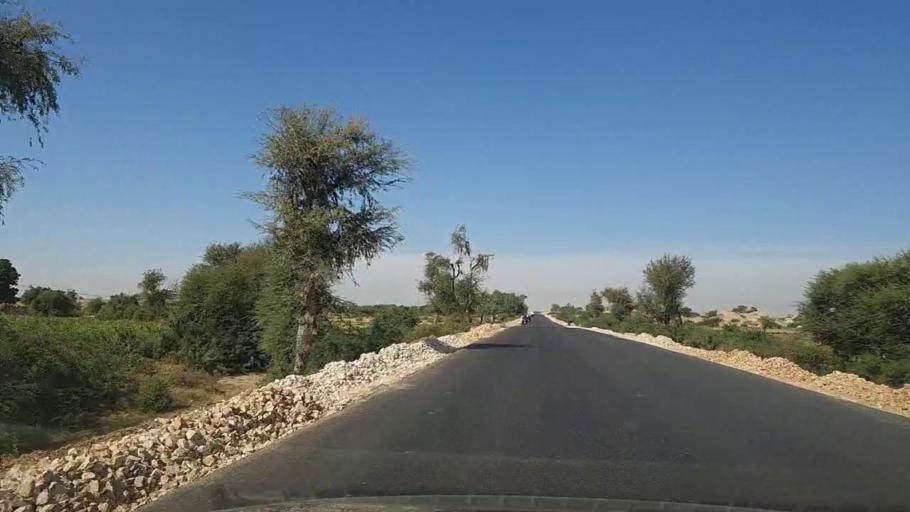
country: PK
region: Sindh
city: Kotri
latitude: 25.2902
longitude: 68.2066
